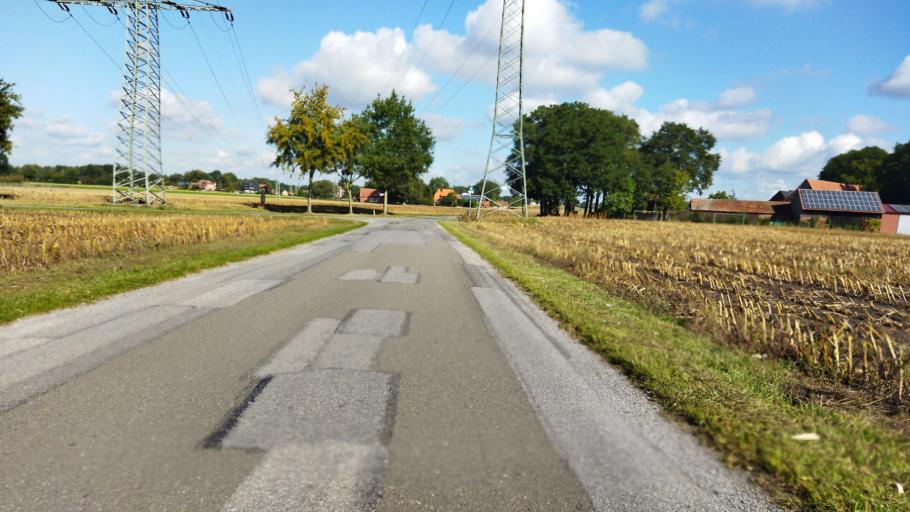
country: DE
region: Lower Saxony
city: Salzbergen
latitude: 52.3081
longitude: 7.3242
